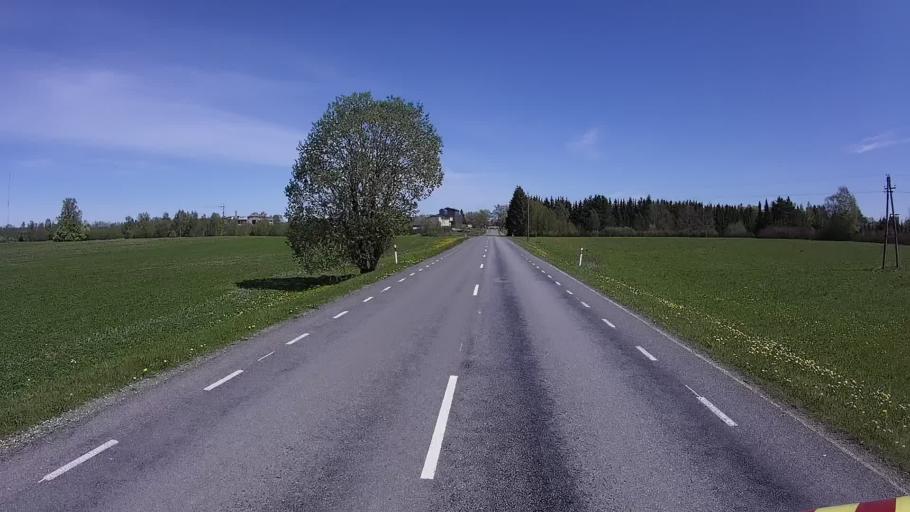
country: EE
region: Raplamaa
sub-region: Kehtna vald
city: Kehtna
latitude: 59.0440
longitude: 25.1081
